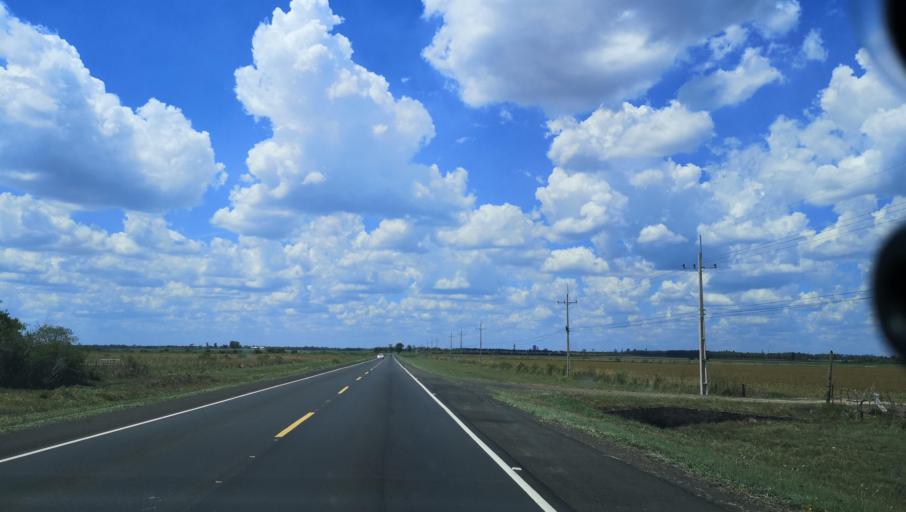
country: PY
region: Itapua
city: General Delgado
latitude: -27.0845
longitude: -56.4825
